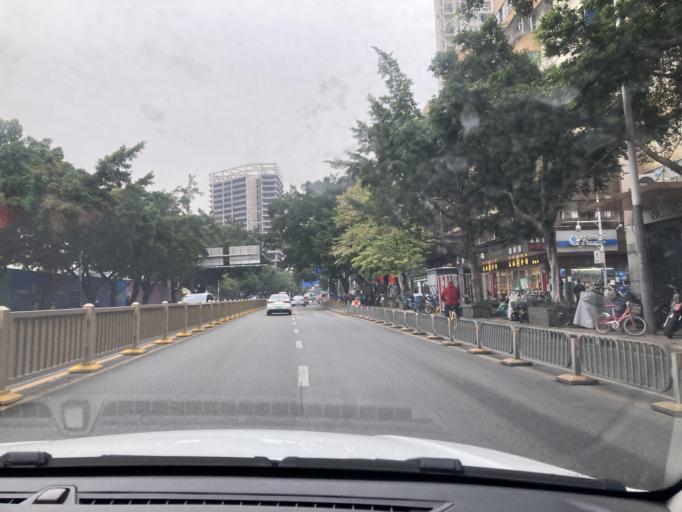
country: CN
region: Guangdong
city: Nantou
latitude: 22.5361
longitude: 113.9144
